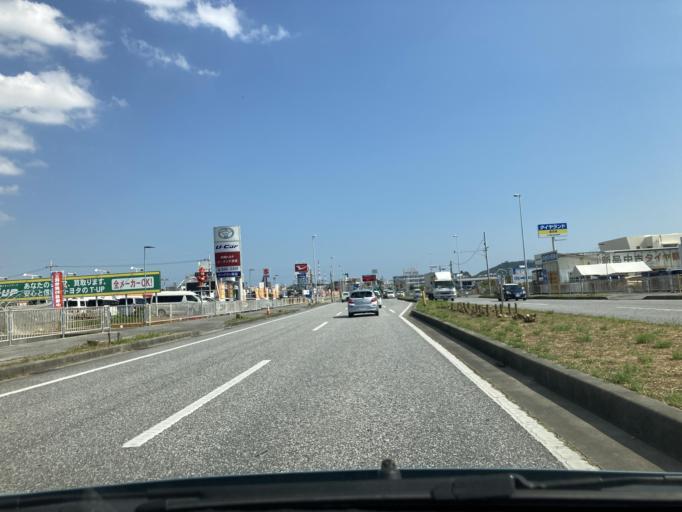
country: JP
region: Okinawa
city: Tomigusuku
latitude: 26.1737
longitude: 127.6590
